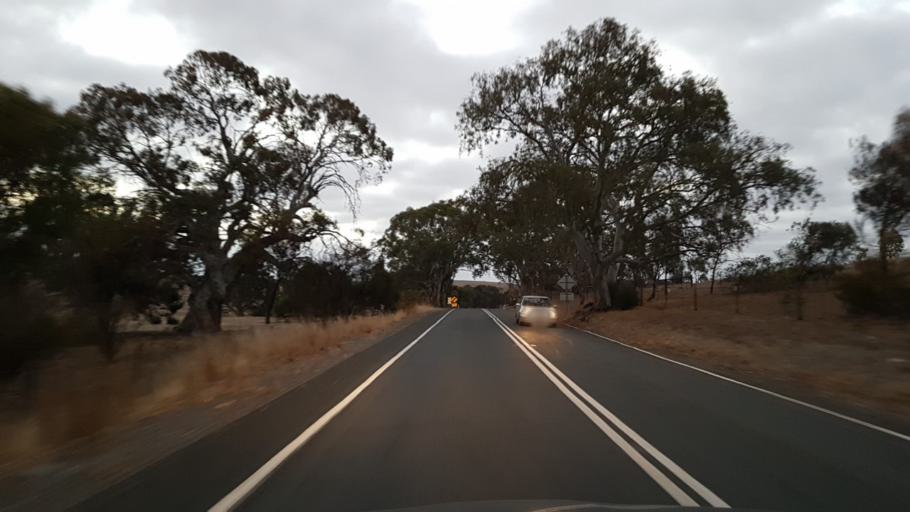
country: AU
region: South Australia
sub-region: Mount Barker
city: Nairne
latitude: -35.0326
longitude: 138.9725
